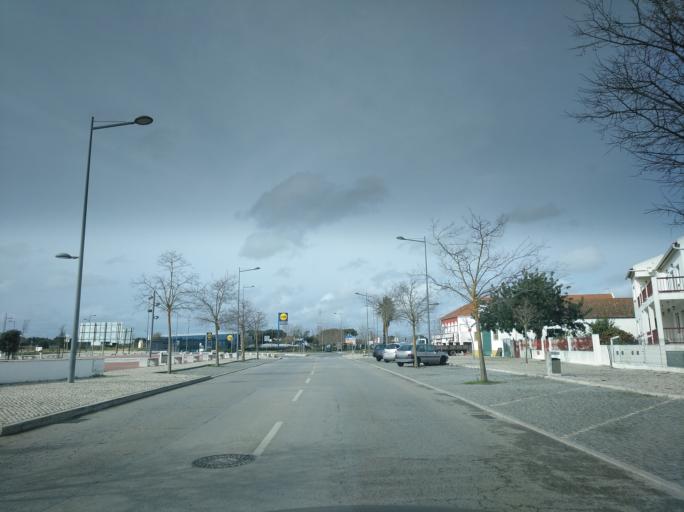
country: PT
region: Setubal
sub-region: Grandola
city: Grandola
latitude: 38.1832
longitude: -8.5674
